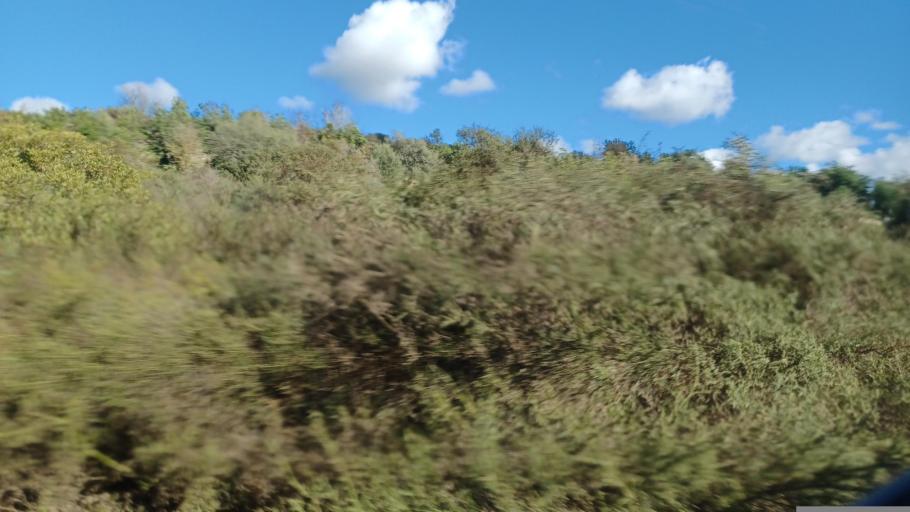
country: CY
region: Limassol
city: Pano Polemidia
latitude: 34.7585
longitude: 32.9791
